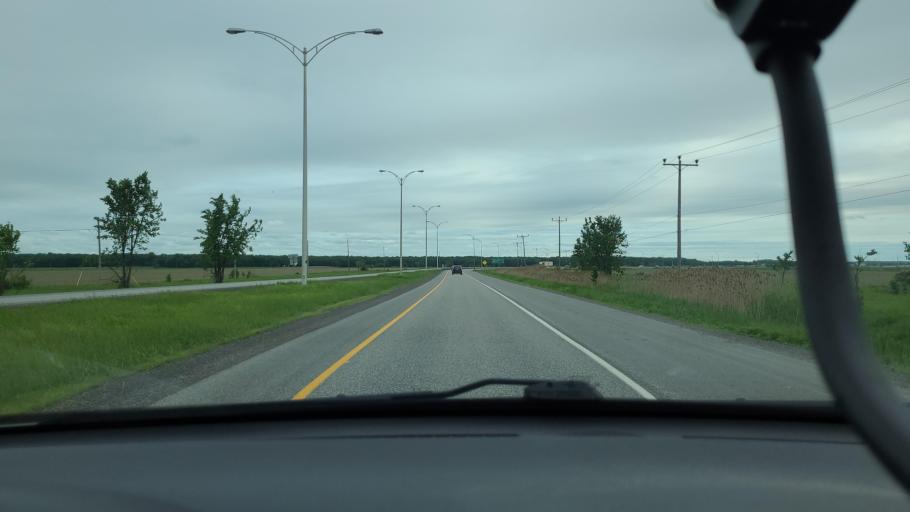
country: CA
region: Quebec
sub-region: Lanaudiere
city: Sainte-Julienne
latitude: 45.9071
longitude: -73.6584
